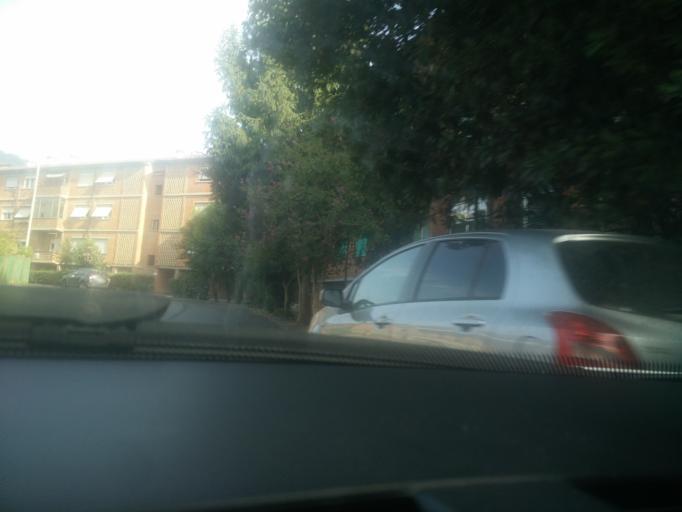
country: IT
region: Tuscany
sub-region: Provincia di Massa-Carrara
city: Carrara
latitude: 44.0600
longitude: 10.0836
